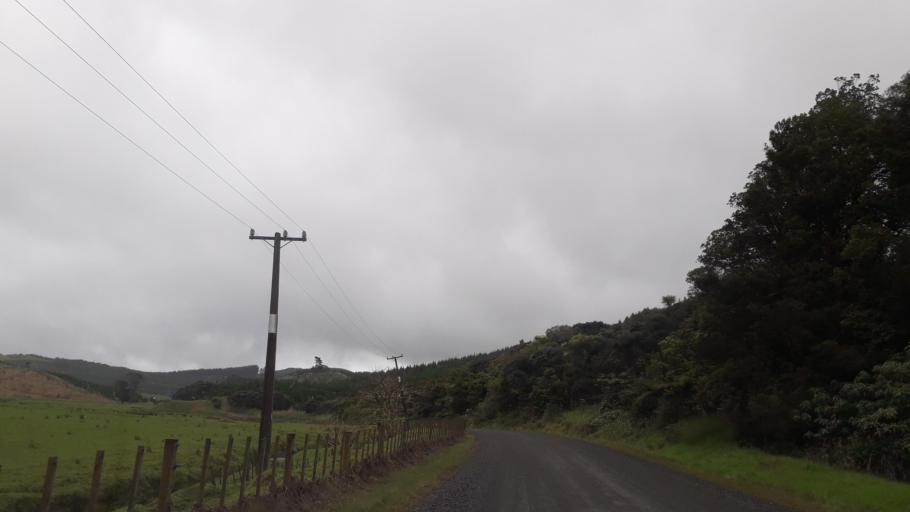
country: NZ
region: Northland
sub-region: Far North District
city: Ahipara
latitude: -35.4275
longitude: 173.3543
